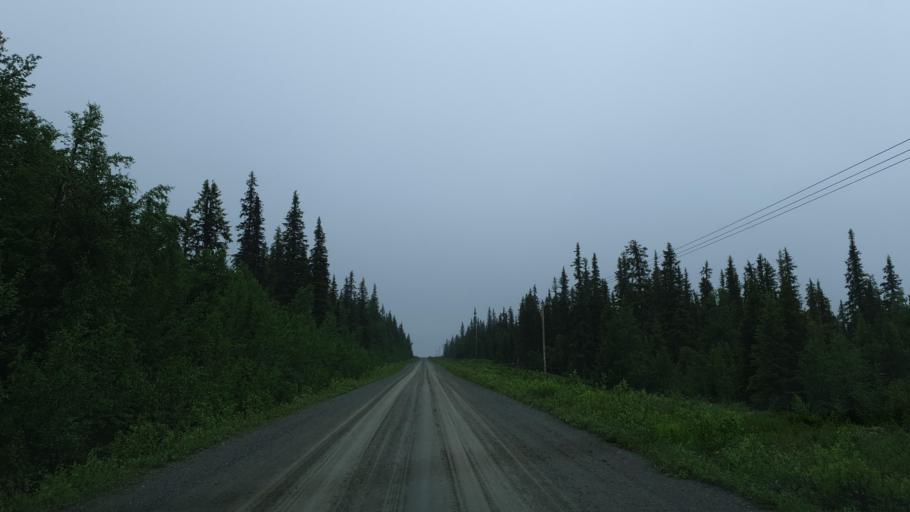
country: SE
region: Vaesterbotten
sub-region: Vilhelmina Kommun
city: Sjoberg
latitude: 65.3194
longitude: 15.9436
